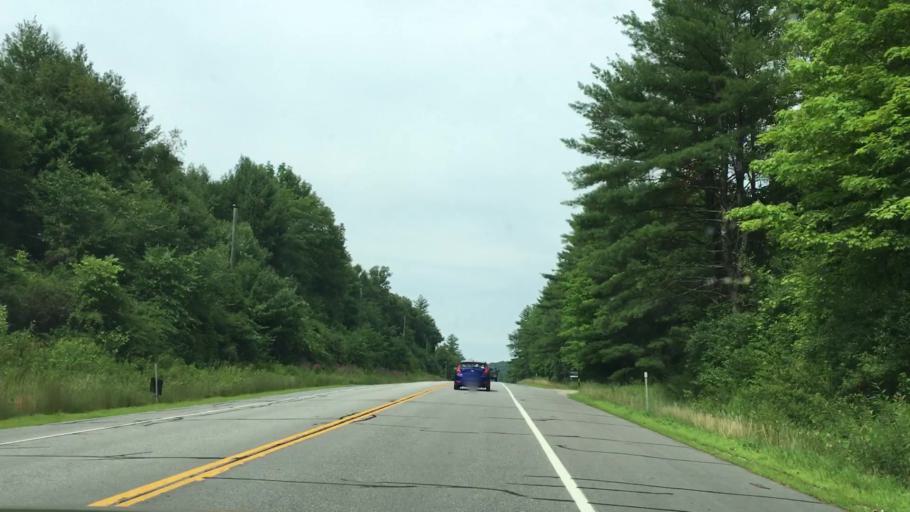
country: US
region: New Hampshire
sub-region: Hillsborough County
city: Antrim
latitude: 43.0533
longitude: -71.9238
